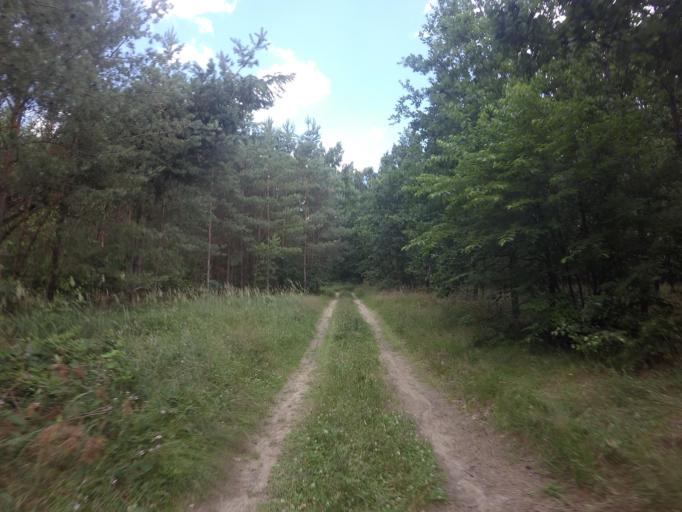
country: PL
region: West Pomeranian Voivodeship
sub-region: Powiat choszczenski
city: Choszczno
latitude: 53.2020
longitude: 15.4881
